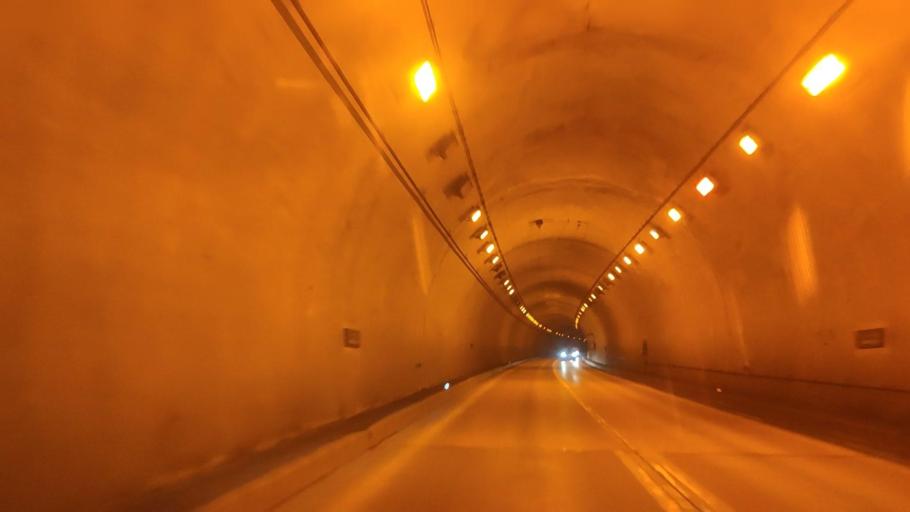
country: JP
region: Tottori
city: Kurayoshi
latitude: 35.3175
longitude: 133.7558
